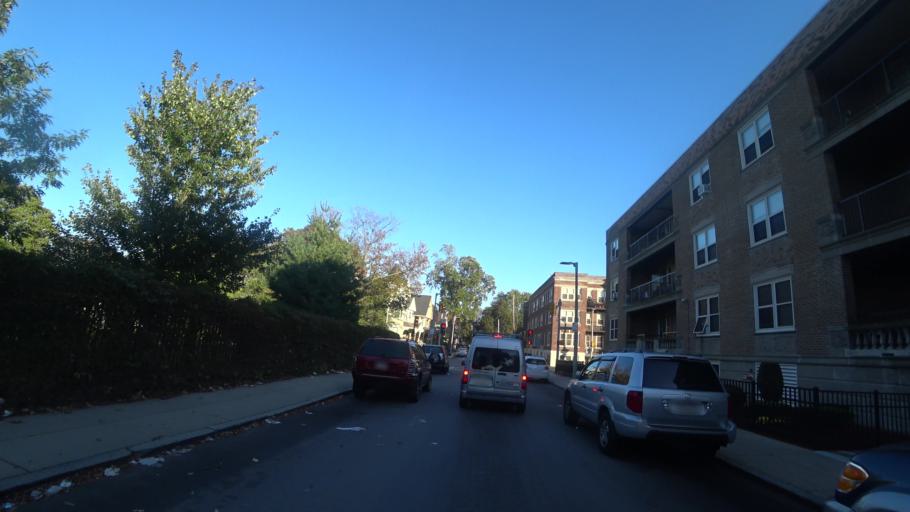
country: US
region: Massachusetts
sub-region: Suffolk County
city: Jamaica Plain
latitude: 42.3136
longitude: -71.0900
